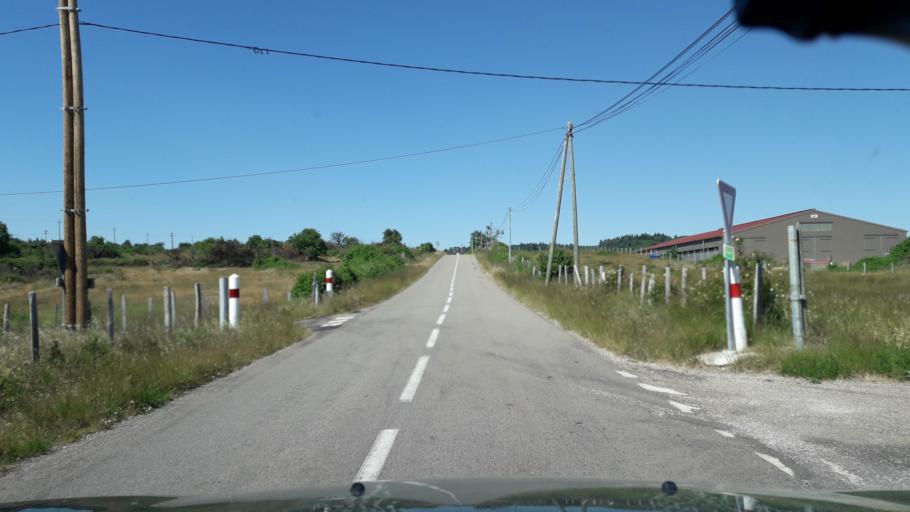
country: FR
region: Rhone-Alpes
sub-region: Departement de l'Ardeche
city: Saint-Priest
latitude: 44.6382
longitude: 4.5564
